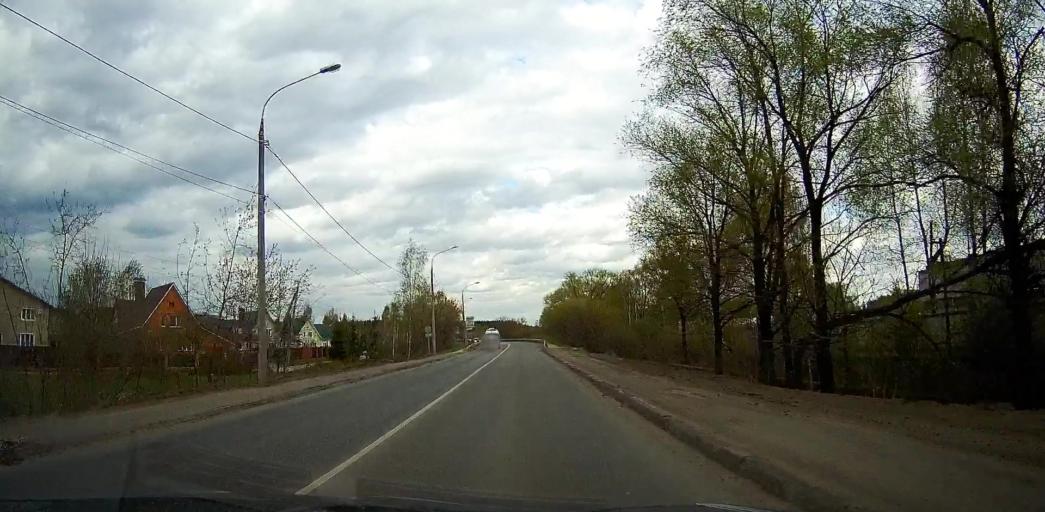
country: RU
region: Moskovskaya
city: Pavlovskiy Posad
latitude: 55.7937
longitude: 38.6514
